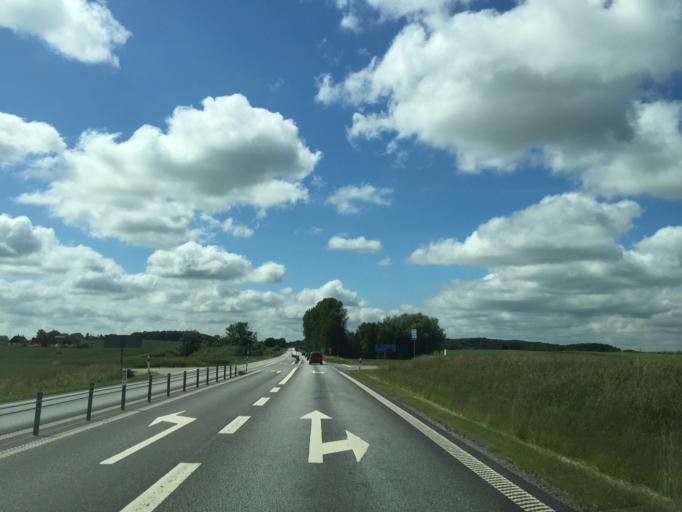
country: SE
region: Skane
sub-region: Skurups Kommun
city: Skurup
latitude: 55.4924
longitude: 13.5268
